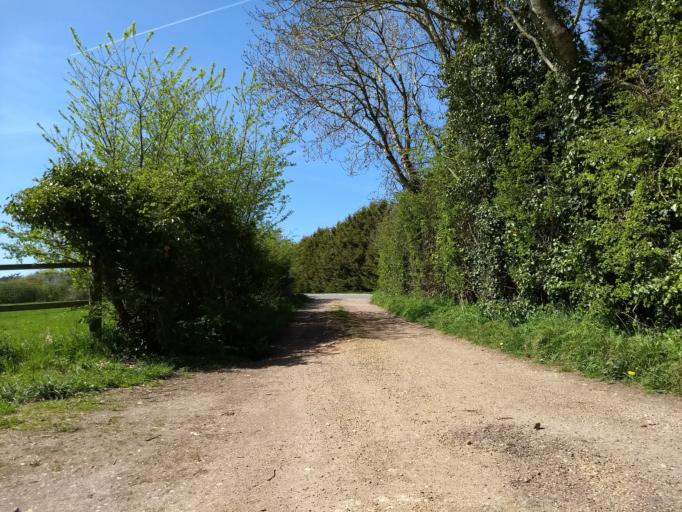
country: GB
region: England
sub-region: Isle of Wight
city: Northwood
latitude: 50.7402
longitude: -1.3012
